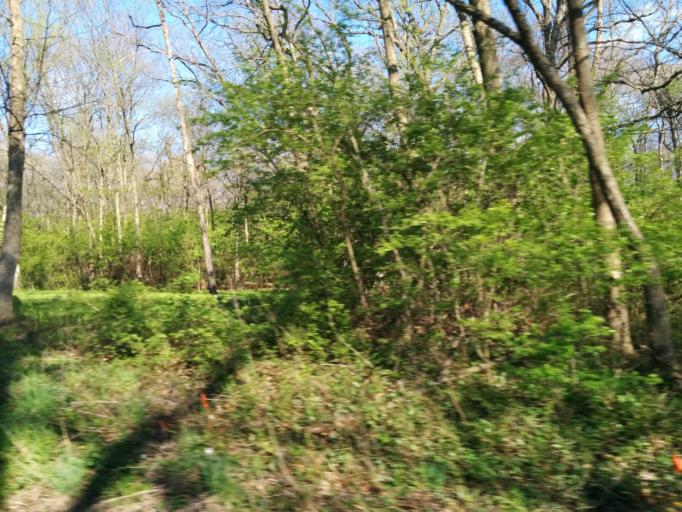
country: US
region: Illinois
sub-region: Cook County
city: Willow Springs
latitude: 41.7296
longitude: -87.8760
